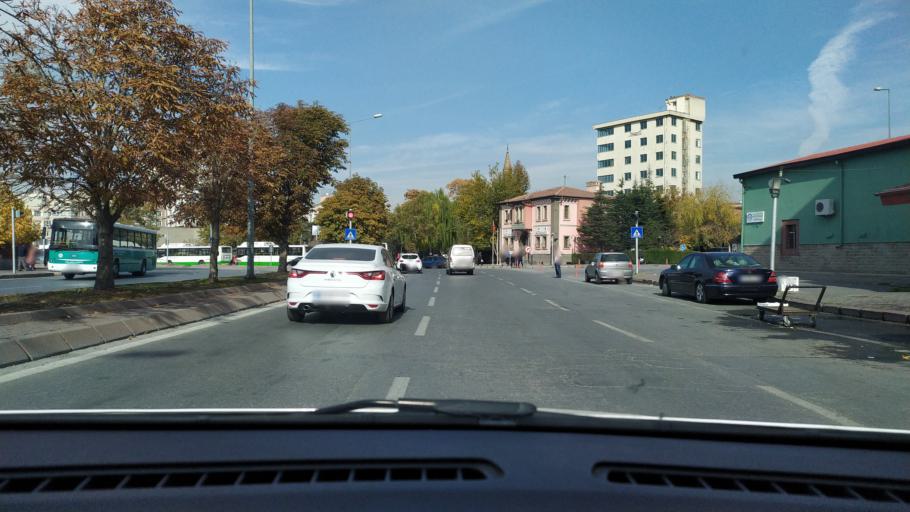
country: TR
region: Kayseri
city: Kayseri
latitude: 38.7160
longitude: 35.4914
